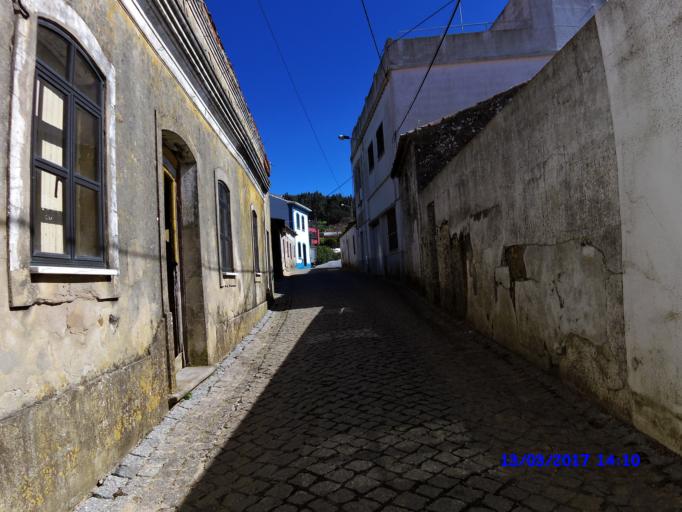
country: PT
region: Faro
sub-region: Monchique
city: Monchique
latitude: 37.3106
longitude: -8.6680
